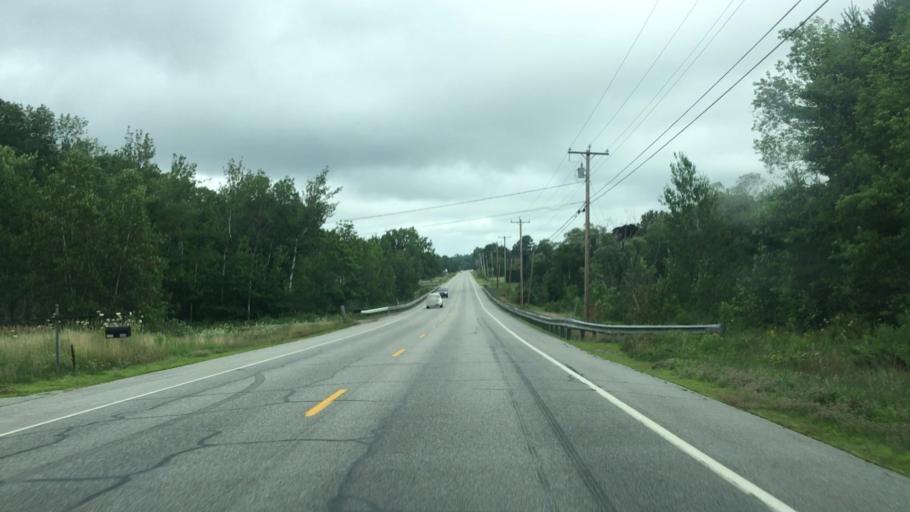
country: US
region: Maine
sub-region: Kennebec County
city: Pittston
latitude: 44.1491
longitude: -69.7436
